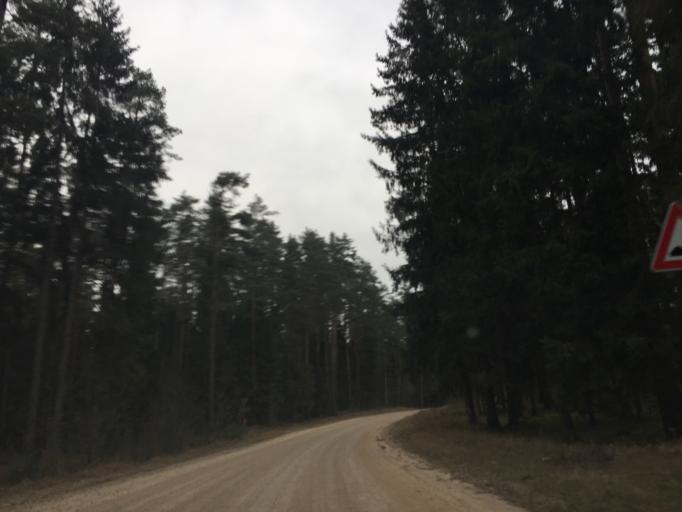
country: LV
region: Cesu Rajons
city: Cesis
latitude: 57.3318
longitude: 25.2568
